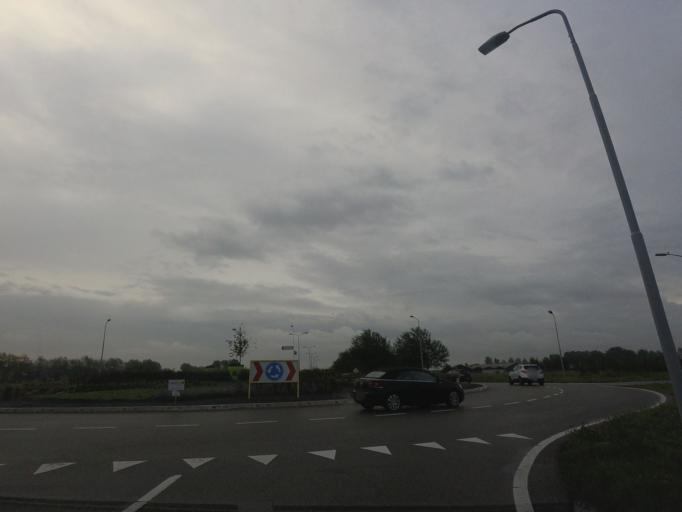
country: NL
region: North Holland
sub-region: Gemeente Bloemendaal
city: Bennebroek
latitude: 52.2991
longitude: 4.6338
